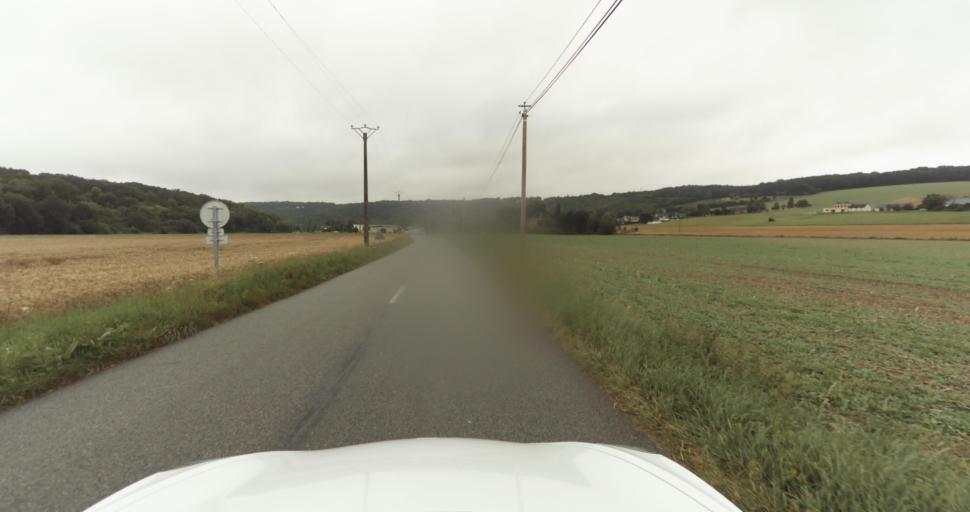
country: FR
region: Haute-Normandie
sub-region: Departement de l'Eure
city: Normanville
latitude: 49.0861
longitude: 1.1384
